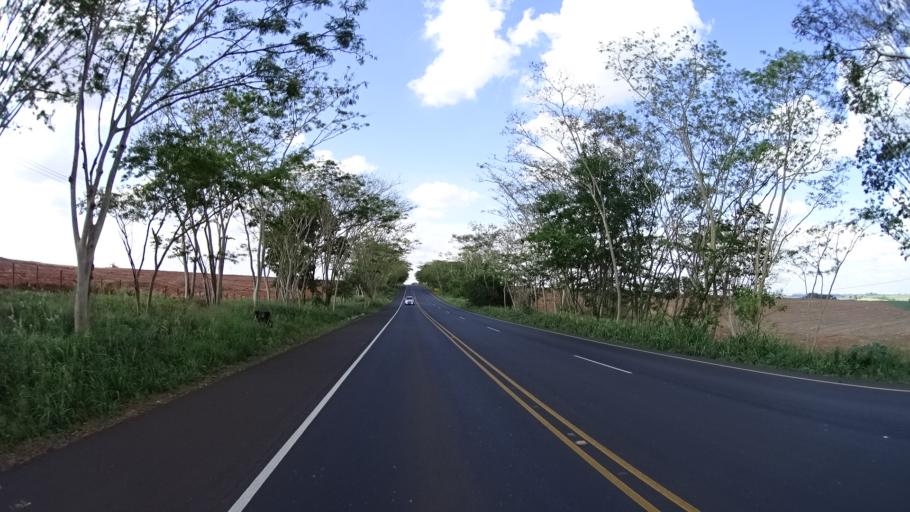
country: BR
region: Sao Paulo
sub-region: Urupes
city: Urupes
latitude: -21.0403
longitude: -49.2430
